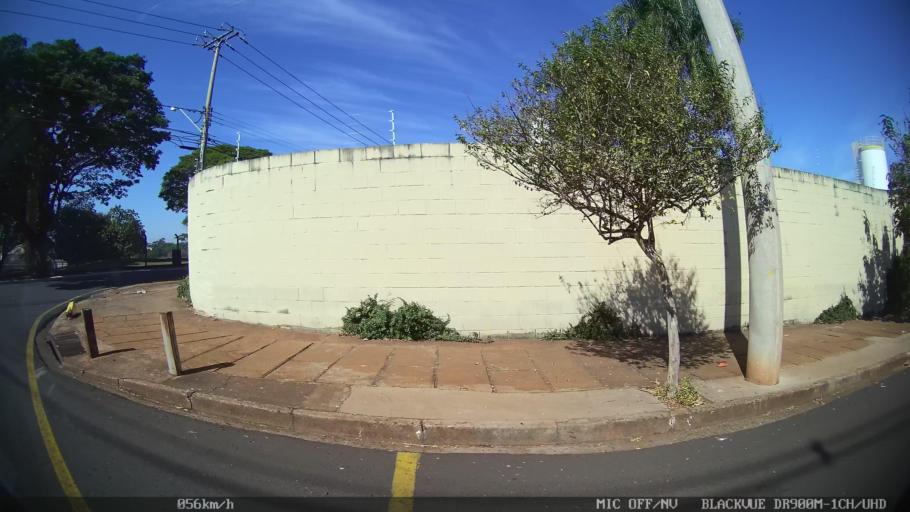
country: BR
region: Sao Paulo
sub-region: Sao Jose Do Rio Preto
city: Sao Jose do Rio Preto
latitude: -20.8114
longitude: -49.4201
